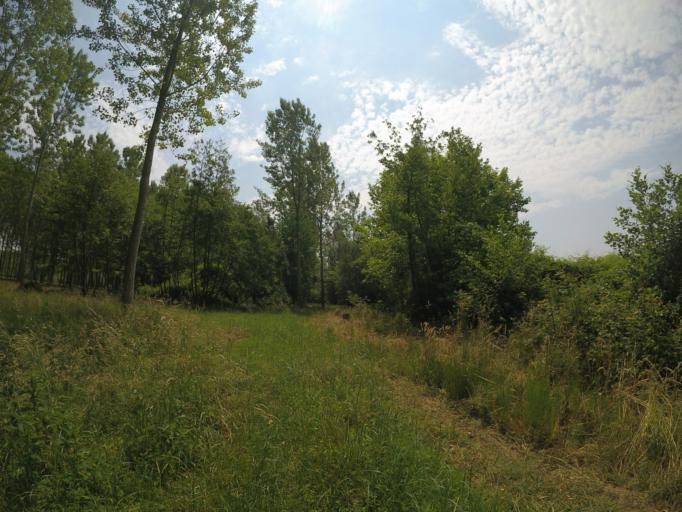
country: IT
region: Friuli Venezia Giulia
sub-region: Provincia di Udine
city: Rivignano
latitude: 45.9120
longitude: 13.0357
